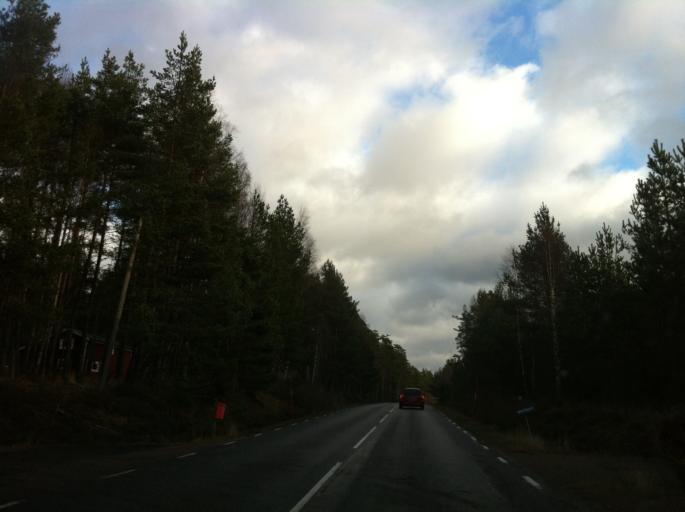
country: SE
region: Kalmar
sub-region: Hultsfreds Kommun
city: Hultsfred
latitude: 57.5215
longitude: 15.7104
